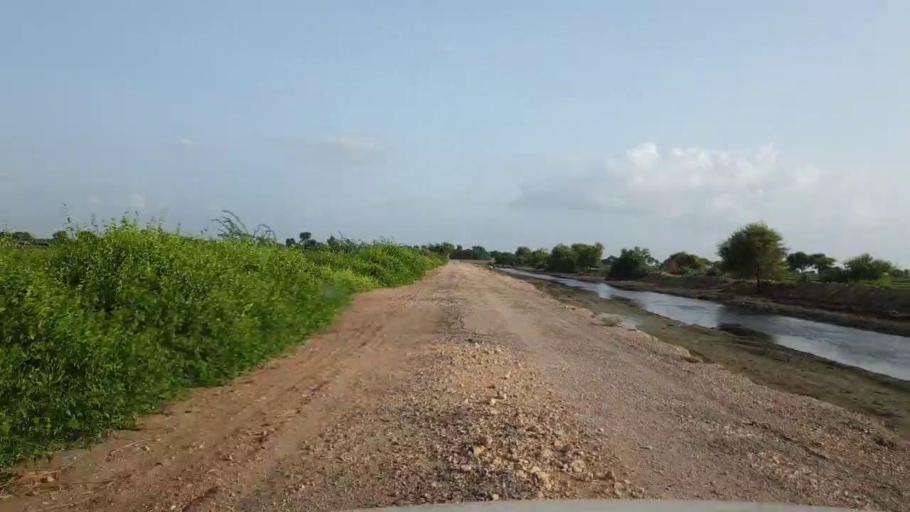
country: PK
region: Sindh
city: Kario
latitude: 24.8415
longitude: 68.6523
